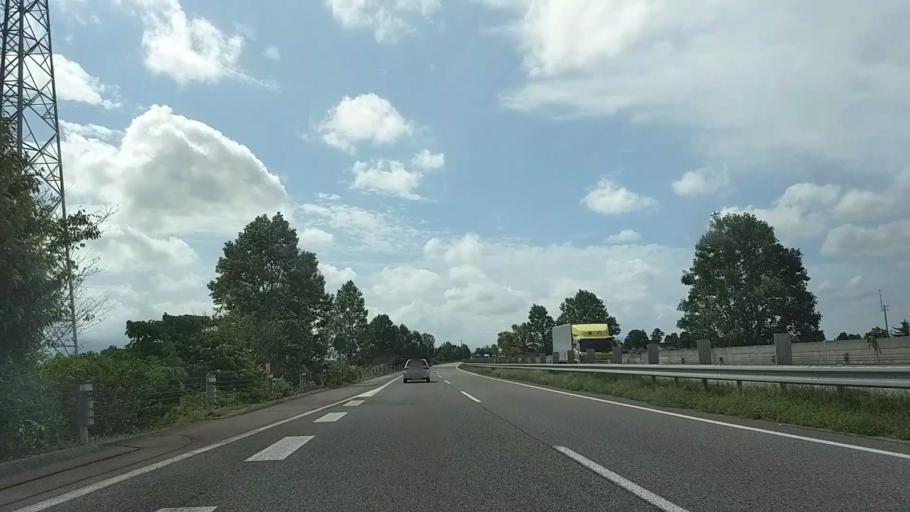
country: JP
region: Toyama
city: Takaoka
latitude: 36.6677
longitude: 137.0290
